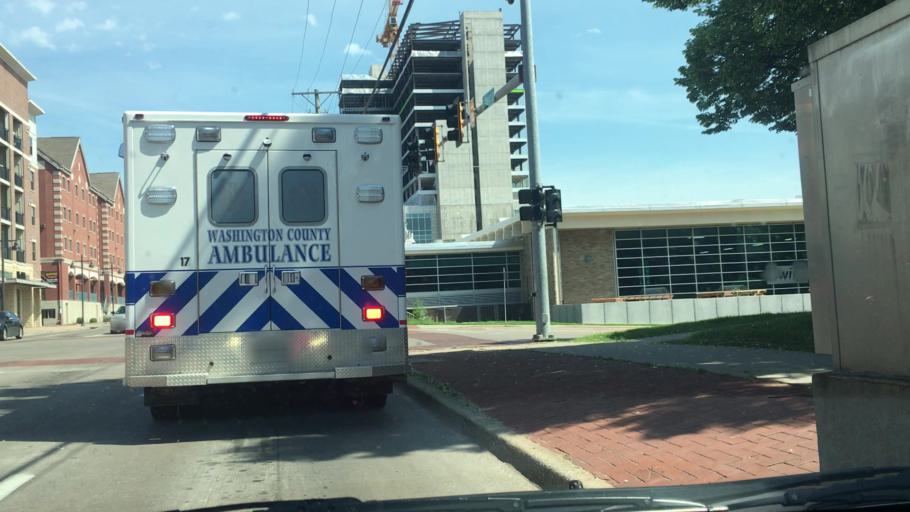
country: US
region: Iowa
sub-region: Johnson County
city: Iowa City
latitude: 41.6575
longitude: -91.5301
